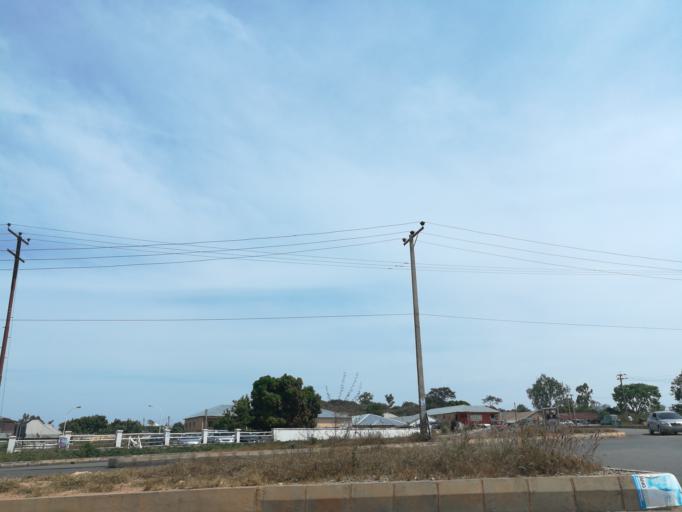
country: NG
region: Plateau
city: Bukuru
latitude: 9.8128
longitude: 8.8660
